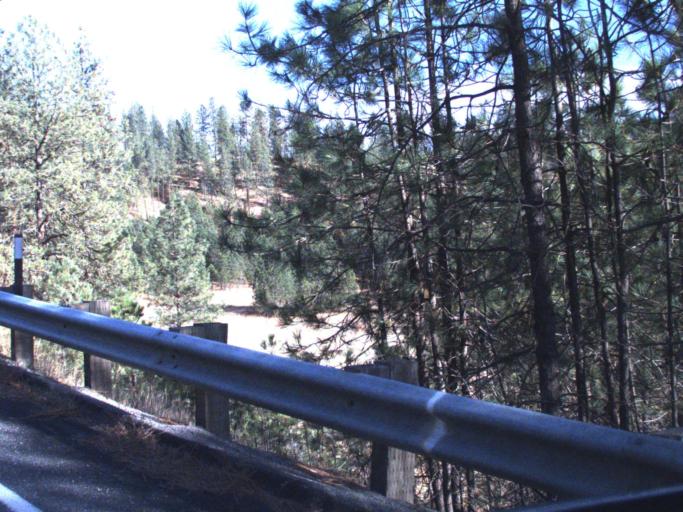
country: US
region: Washington
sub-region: Stevens County
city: Kettle Falls
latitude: 48.5795
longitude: -118.0785
